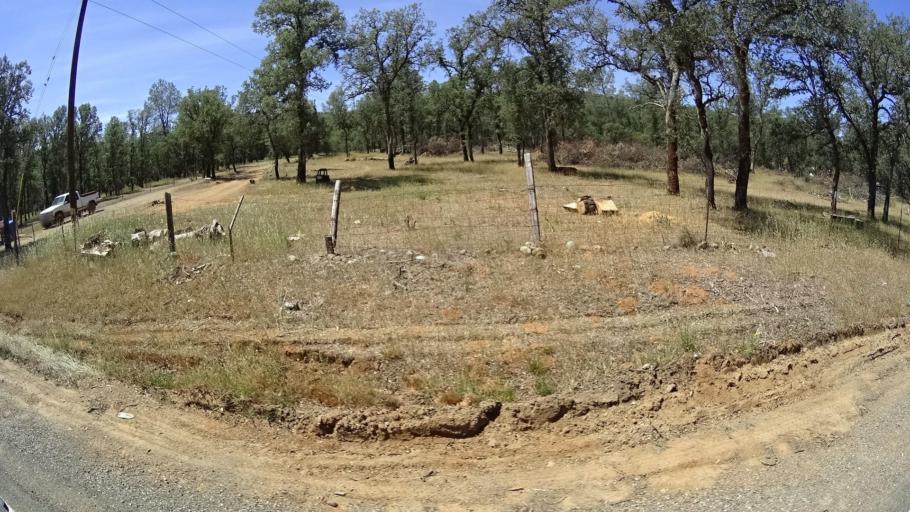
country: US
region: California
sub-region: Lake County
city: Middletown
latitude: 38.7253
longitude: -122.5484
